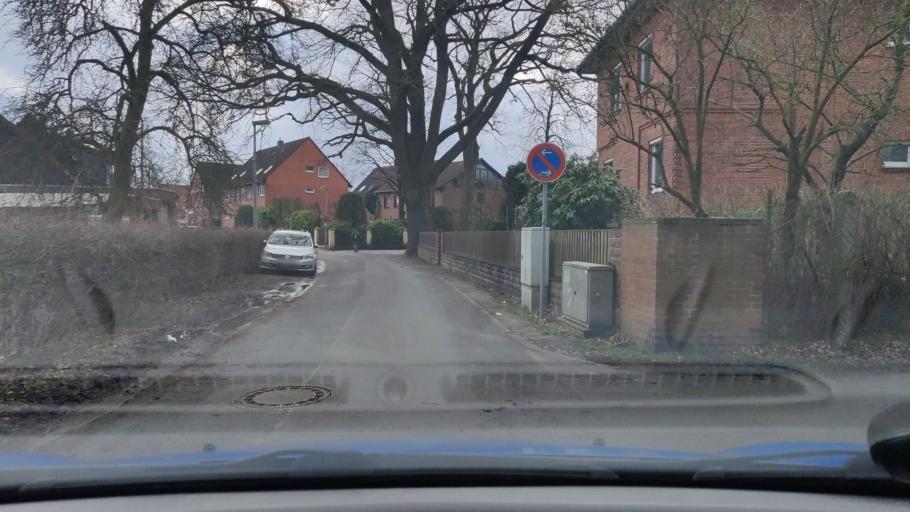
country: DE
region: Lower Saxony
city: Langenhagen
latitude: 52.4767
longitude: 9.7305
